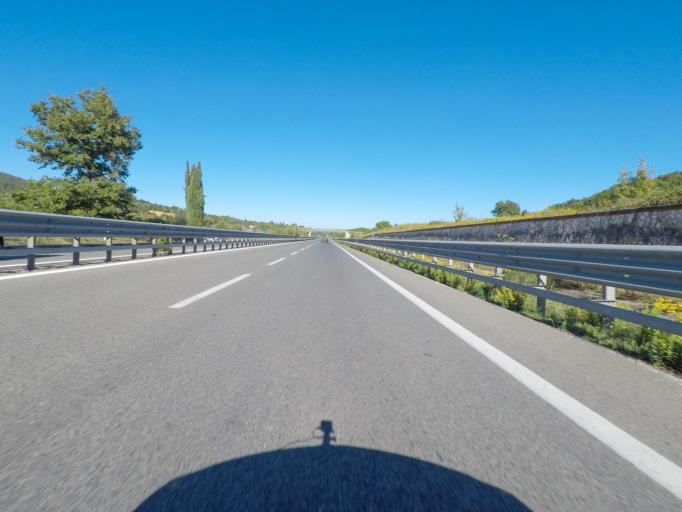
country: IT
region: Tuscany
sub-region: Provincia di Grosseto
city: Campagnatico
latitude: 42.8750
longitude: 11.2098
